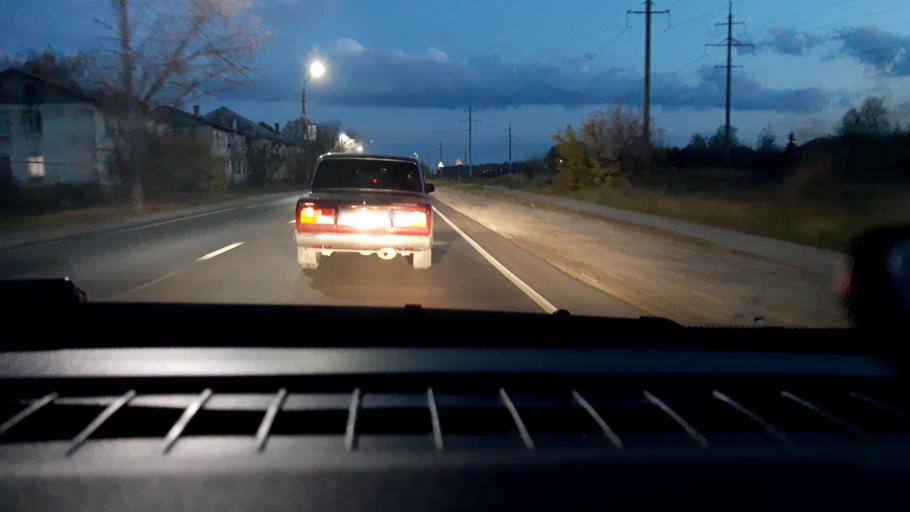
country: RU
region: Nizjnij Novgorod
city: Novaya Balakhna
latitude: 56.4819
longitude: 43.6019
